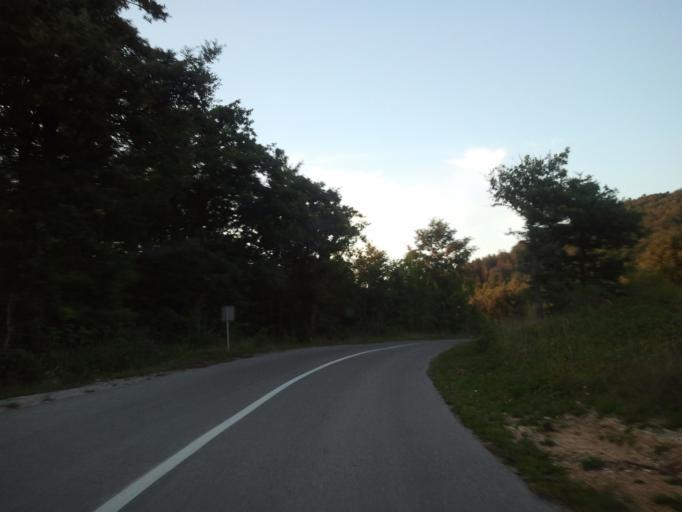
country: HR
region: Zadarska
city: Obrovac
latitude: 44.4227
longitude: 15.6603
